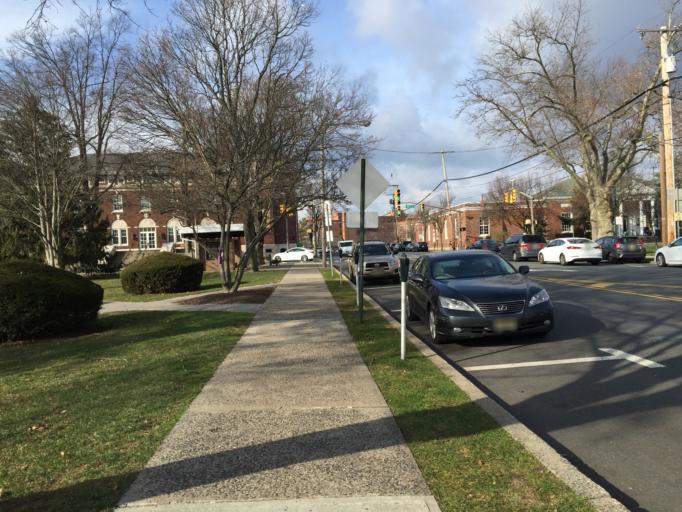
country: US
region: New Jersey
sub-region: Union County
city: Summit
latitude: 40.7160
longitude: -74.3587
